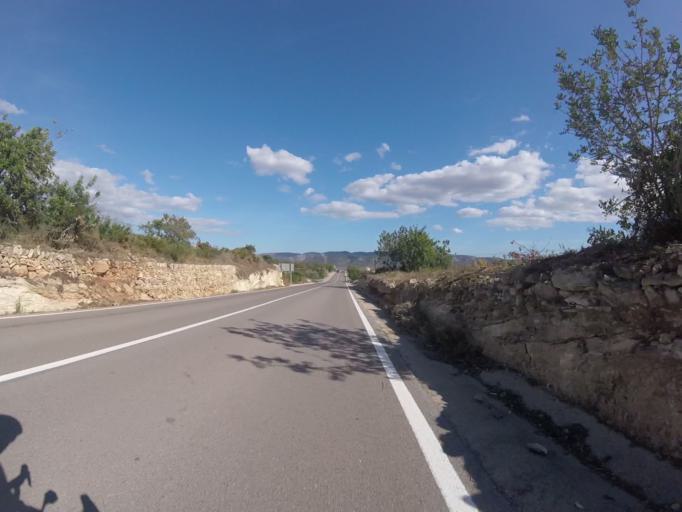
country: ES
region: Valencia
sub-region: Provincia de Castello
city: Alcala de Xivert
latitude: 40.3021
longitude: 0.1928
